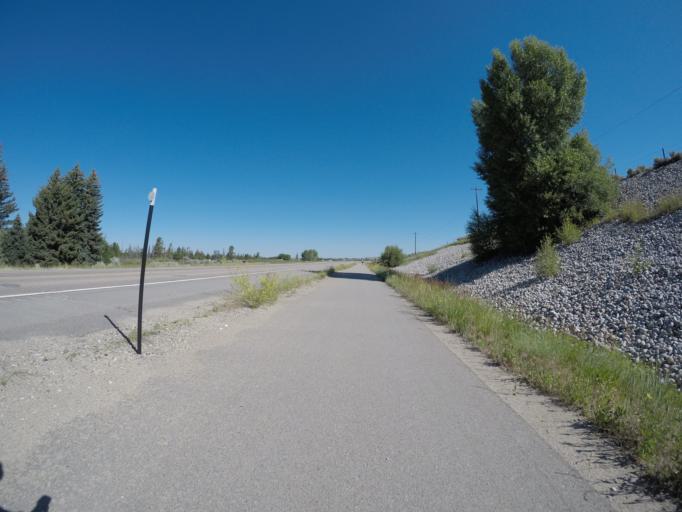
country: US
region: Wyoming
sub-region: Sublette County
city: Pinedale
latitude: 42.8497
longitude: -109.8494
